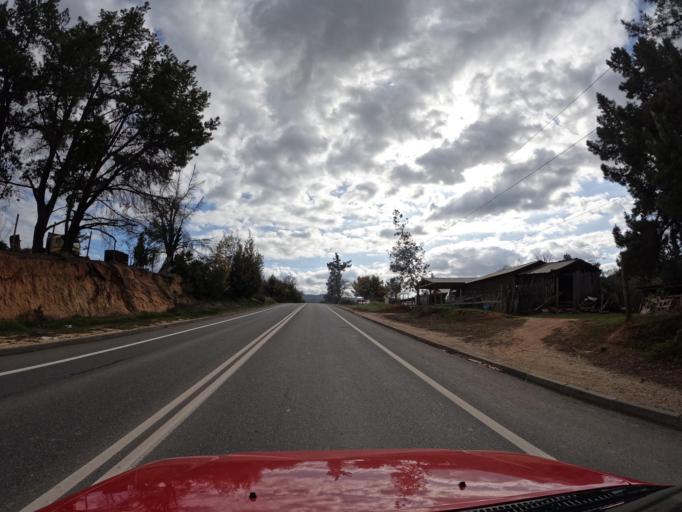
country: CL
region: Maule
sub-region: Provincia de Talca
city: Constitucion
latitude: -35.5565
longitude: -72.1209
